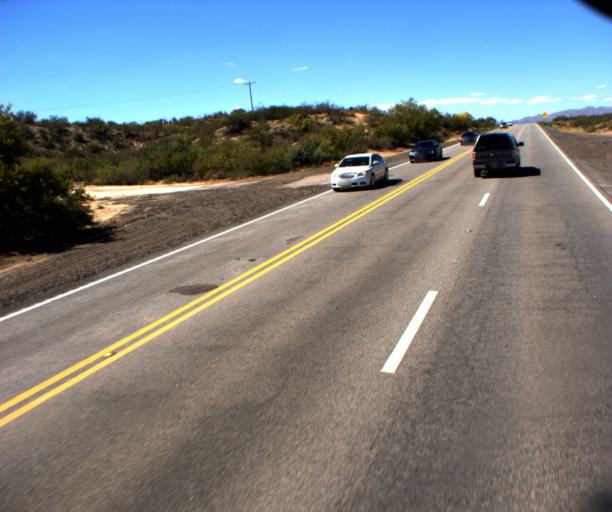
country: US
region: Arizona
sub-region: Yavapai County
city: Bagdad
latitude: 34.8053
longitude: -113.6259
